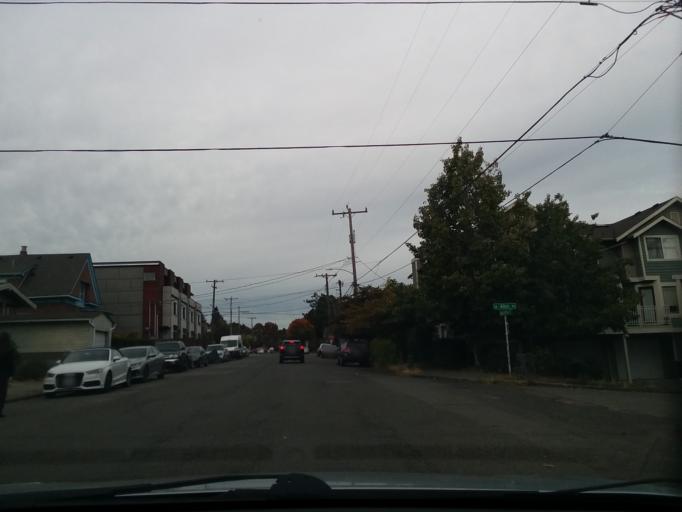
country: US
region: Washington
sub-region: King County
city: Seattle
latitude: 47.6605
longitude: -122.3446
